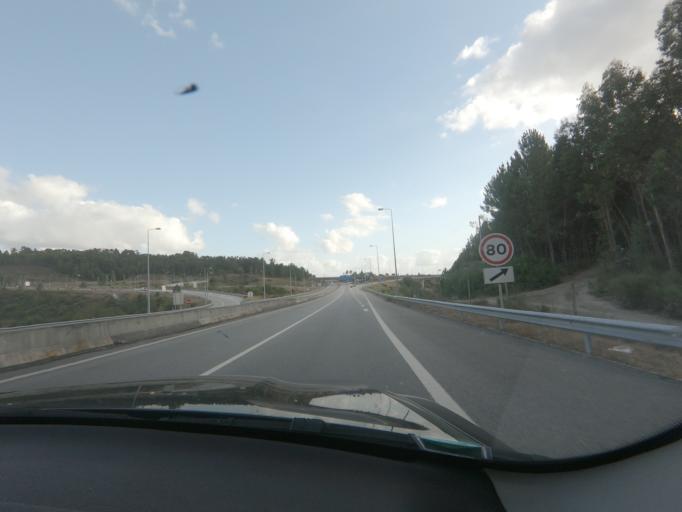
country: PT
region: Viseu
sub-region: Viseu
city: Viseu
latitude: 40.6290
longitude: -7.9605
